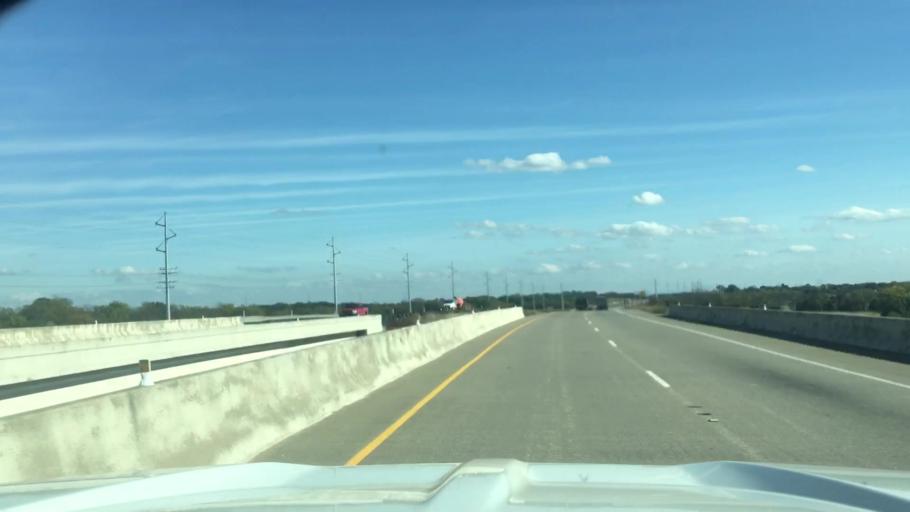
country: US
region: Texas
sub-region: Denton County
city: Denton
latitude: 33.2580
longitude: -97.1100
